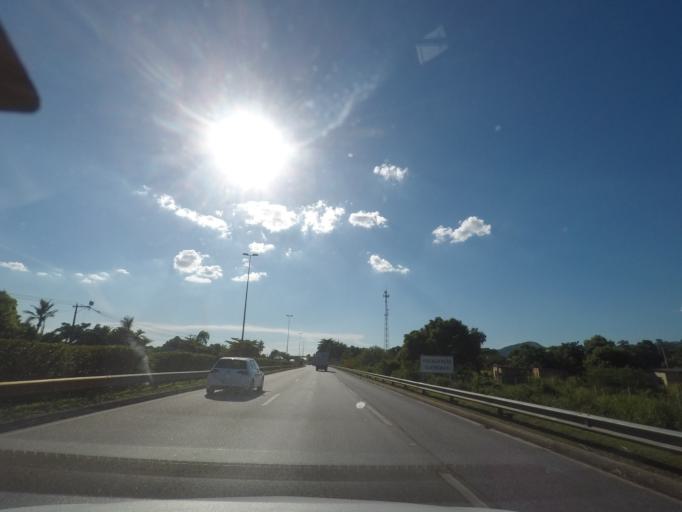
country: BR
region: Rio de Janeiro
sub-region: Petropolis
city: Petropolis
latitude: -22.6463
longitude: -43.2037
